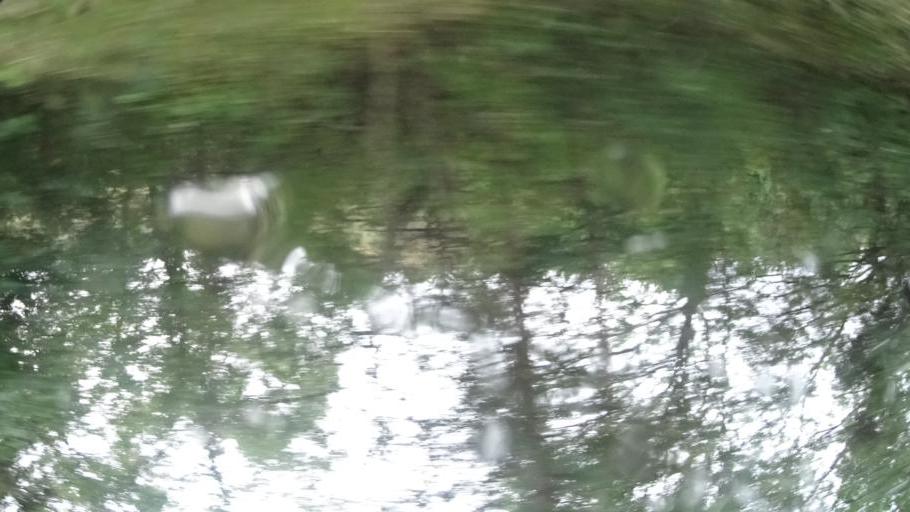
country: DE
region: Thuringia
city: Rittersdorf
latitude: 50.8357
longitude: 11.2249
